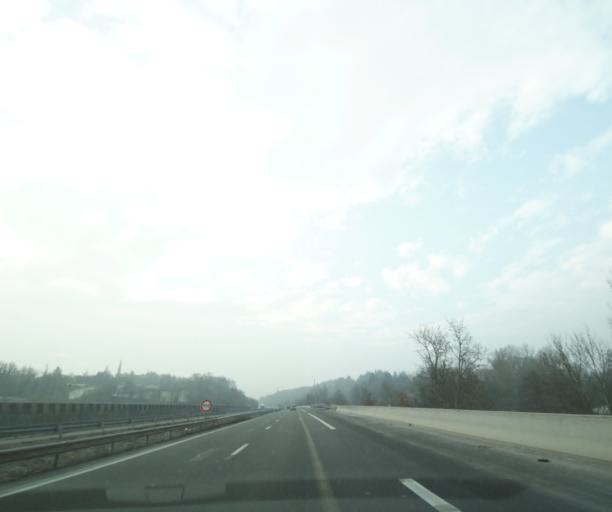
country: FR
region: Rhone-Alpes
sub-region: Departement du Rhone
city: Lissieu
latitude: 45.8612
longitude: 4.7412
